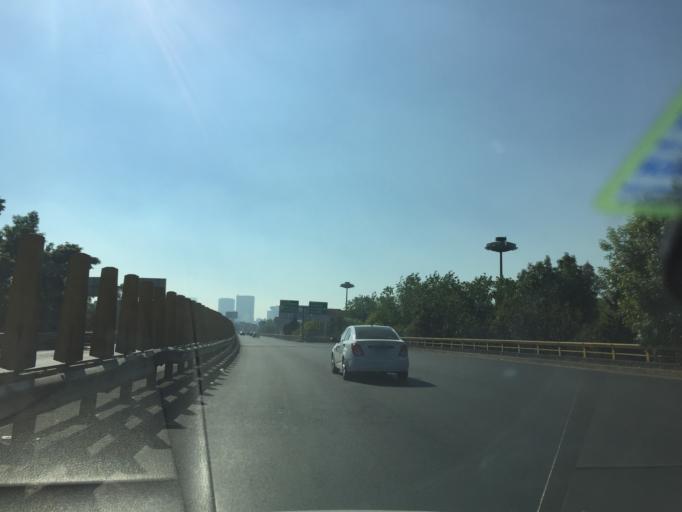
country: MX
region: Mexico City
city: Azcapotzalco
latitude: 19.4608
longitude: -99.1901
